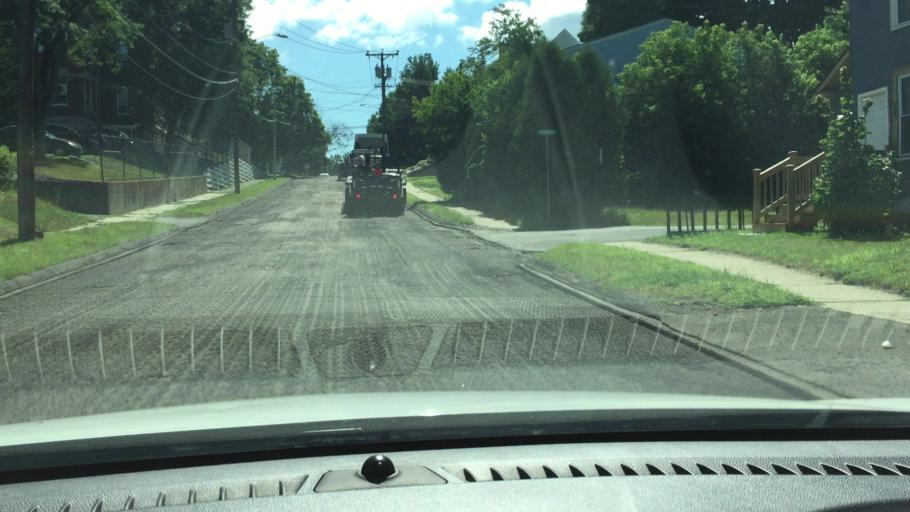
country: US
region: Massachusetts
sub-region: Berkshire County
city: Pittsfield
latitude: 42.4435
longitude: -73.2595
